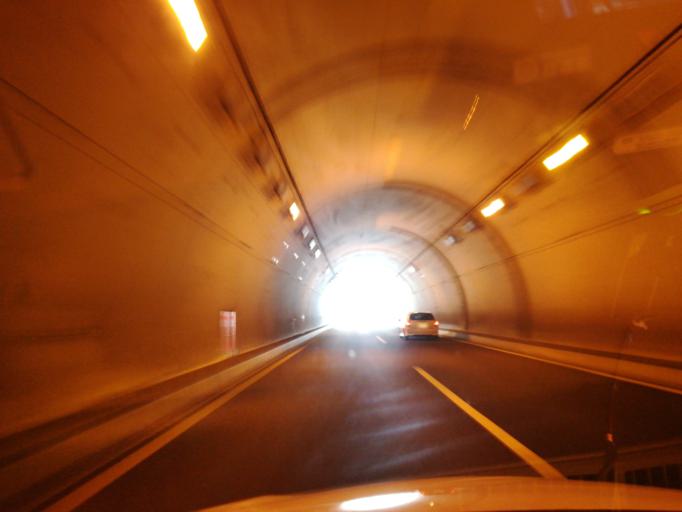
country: JP
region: Kochi
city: Kochi-shi
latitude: 33.7753
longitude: 133.6606
